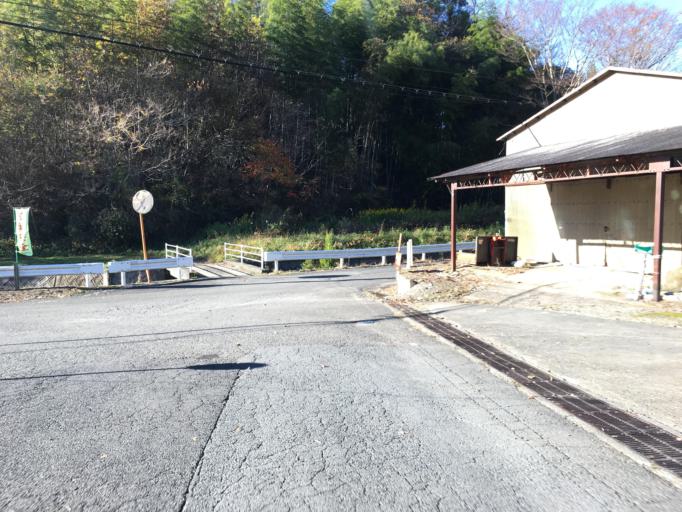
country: JP
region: Fukushima
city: Ishikawa
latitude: 37.2286
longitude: 140.5186
